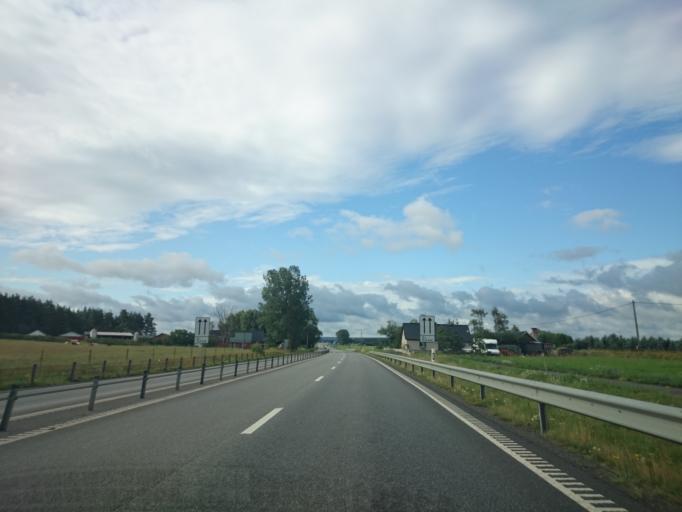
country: SE
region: Skane
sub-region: Kristianstads Kommun
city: Norra Asum
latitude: 55.9647
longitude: 14.0714
